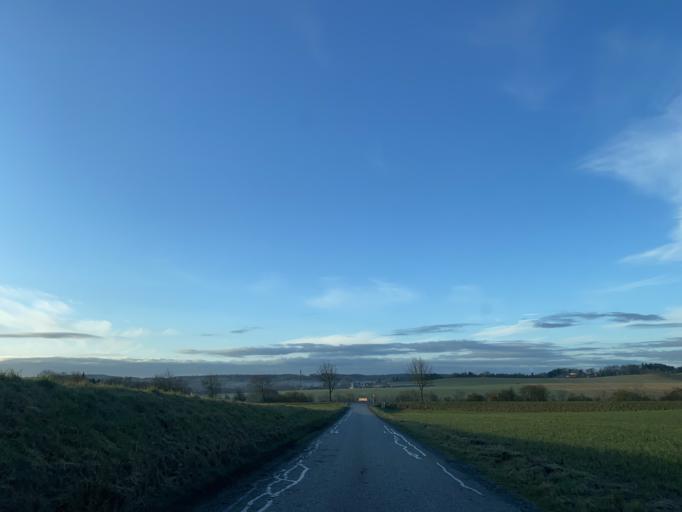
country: DK
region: Central Jutland
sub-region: Favrskov Kommune
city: Hammel
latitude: 56.2403
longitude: 9.7384
